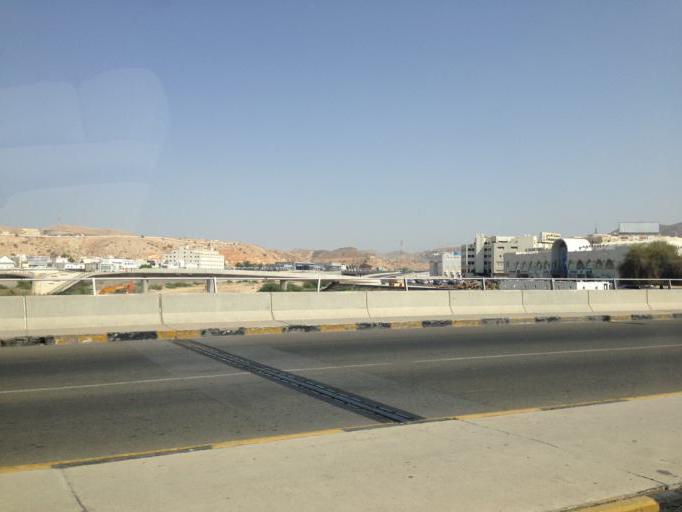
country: OM
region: Muhafazat Masqat
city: Muscat
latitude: 23.6154
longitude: 58.4941
